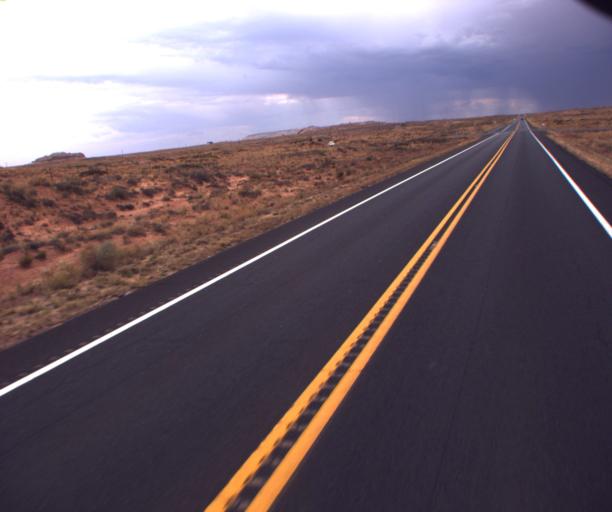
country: US
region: Arizona
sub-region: Coconino County
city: Kaibito
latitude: 36.3070
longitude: -110.9669
